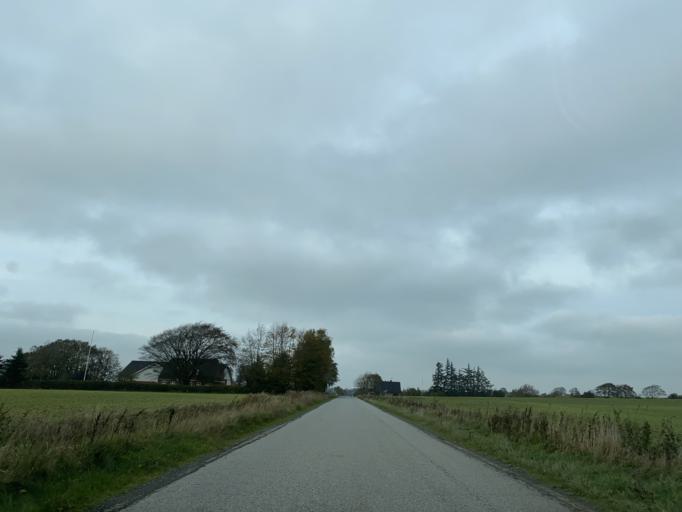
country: DK
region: South Denmark
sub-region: Haderslev Kommune
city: Starup
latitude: 55.1737
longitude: 9.5177
